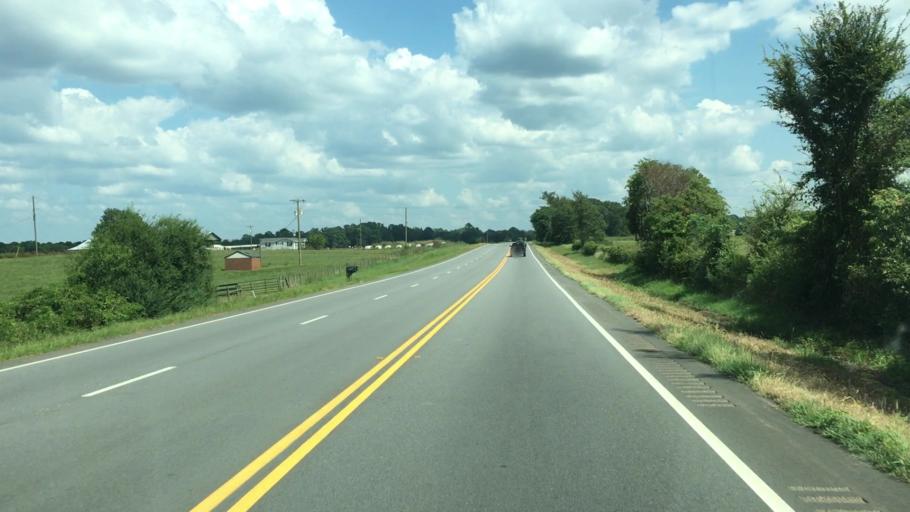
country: US
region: Georgia
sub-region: Putnam County
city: Jefferson
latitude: 33.4742
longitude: -83.4281
